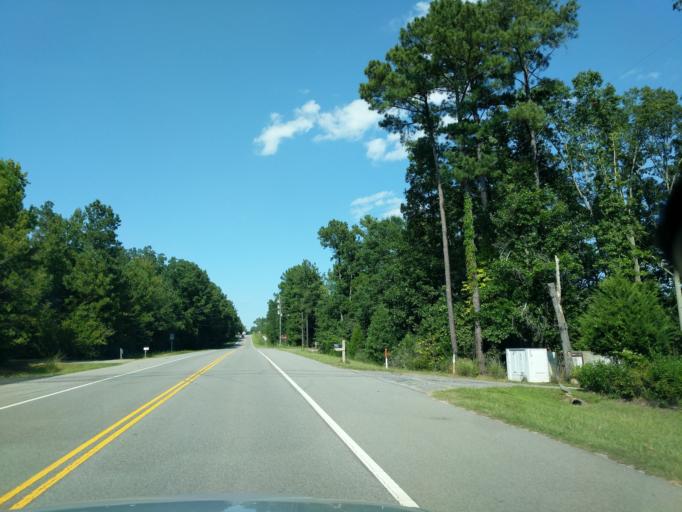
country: US
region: South Carolina
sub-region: Newberry County
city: Prosperity
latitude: 34.1035
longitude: -81.5677
